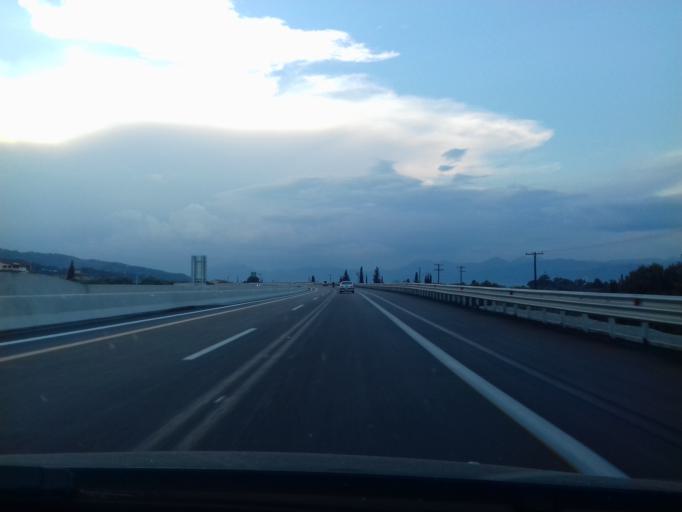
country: GR
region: West Greece
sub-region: Nomos Achaias
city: Selianitika
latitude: 38.2741
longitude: 22.0405
